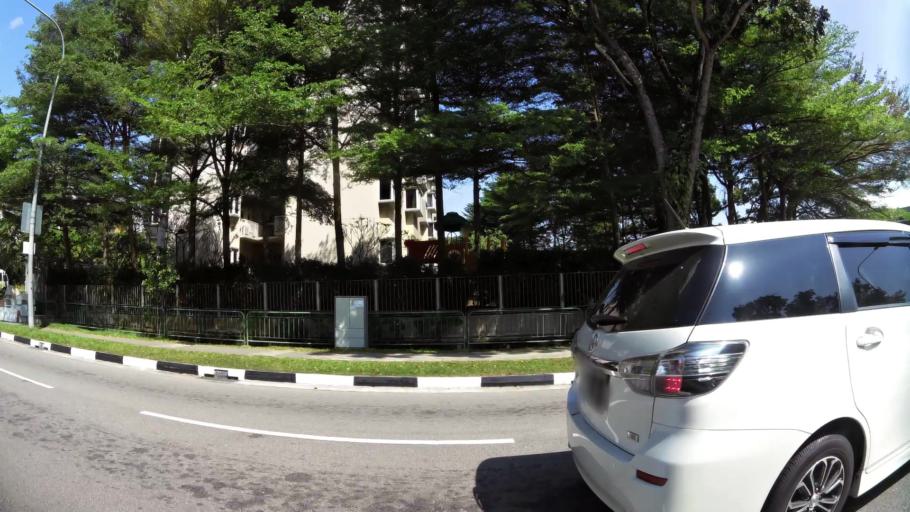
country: SG
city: Singapore
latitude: 1.3840
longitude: 103.8428
